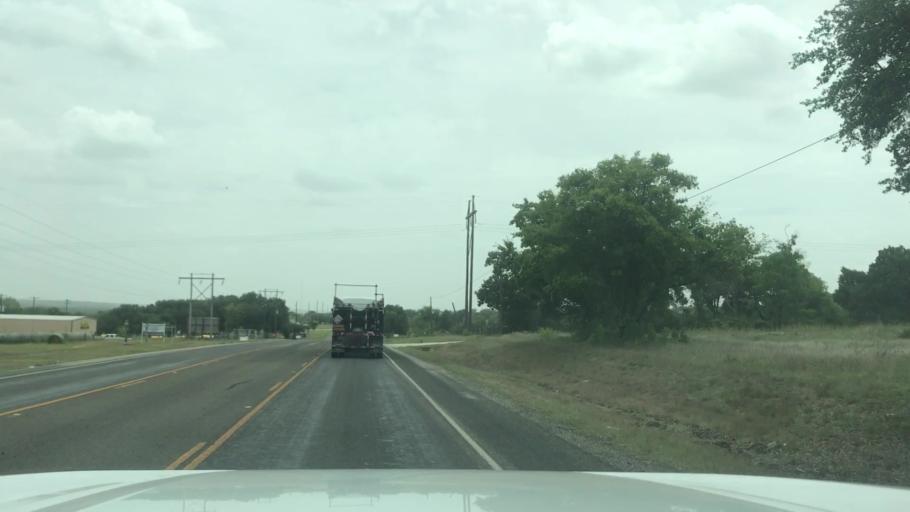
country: US
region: Texas
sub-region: Bosque County
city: Clifton
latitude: 31.7671
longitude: -97.5678
